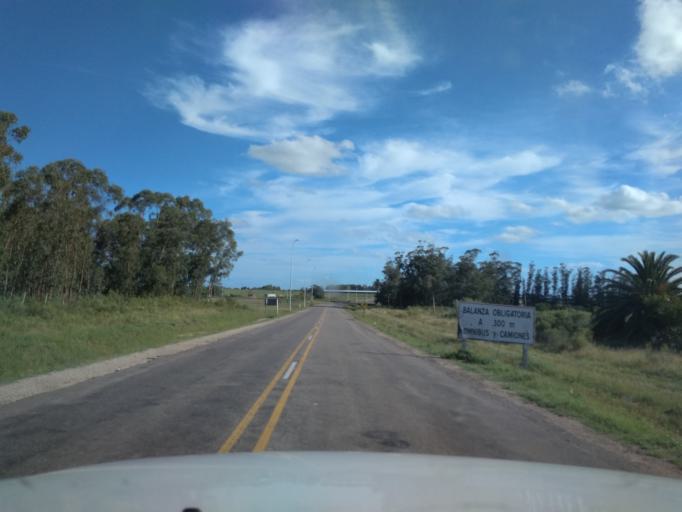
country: UY
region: Canelones
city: San Ramon
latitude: -34.2400
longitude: -55.9258
